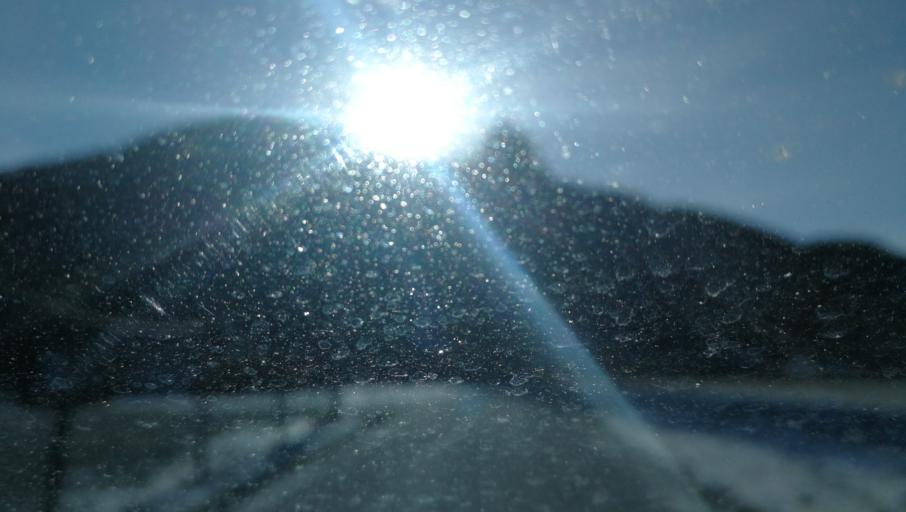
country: NO
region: Rogaland
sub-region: Hjelmeland
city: Hjelmelandsvagen
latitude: 59.1302
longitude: 6.2736
